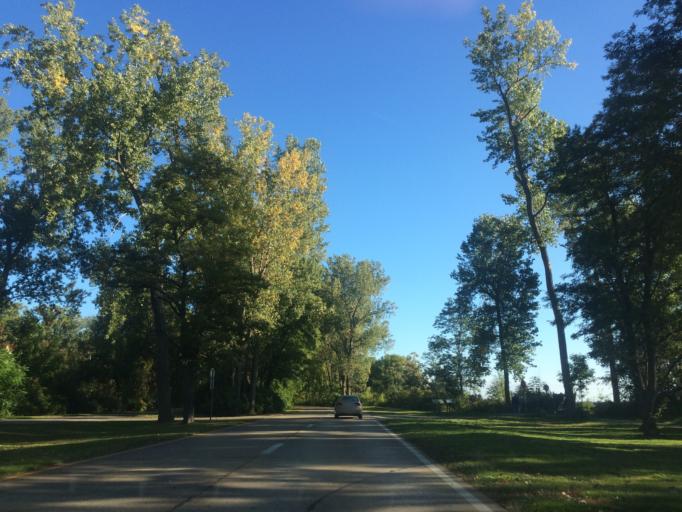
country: US
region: Pennsylvania
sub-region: Erie County
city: Erie
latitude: 42.1262
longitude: -80.1460
